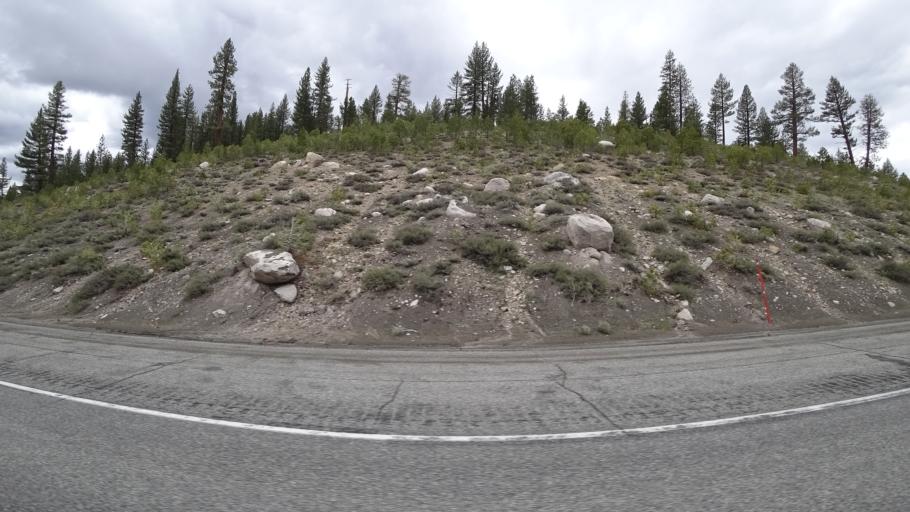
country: US
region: California
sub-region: Mono County
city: Mammoth Lakes
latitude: 37.7621
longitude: -118.9951
